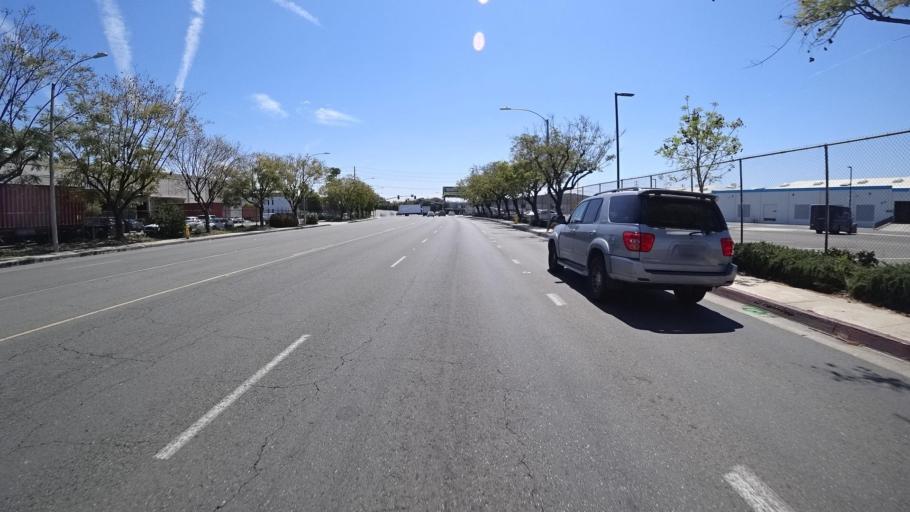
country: US
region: California
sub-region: Los Angeles County
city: La Puente
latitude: 34.0164
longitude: -117.9541
